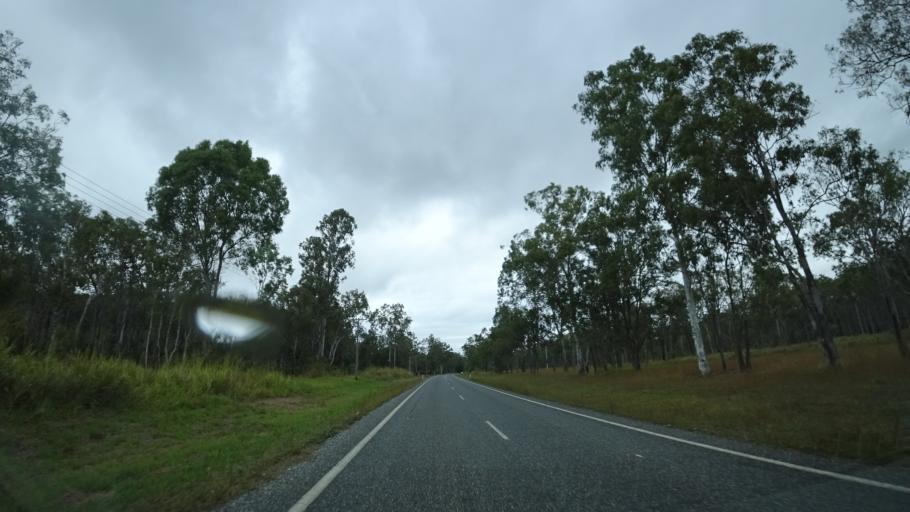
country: AU
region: Queensland
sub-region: Cairns
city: Port Douglas
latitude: -16.7287
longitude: 145.3525
